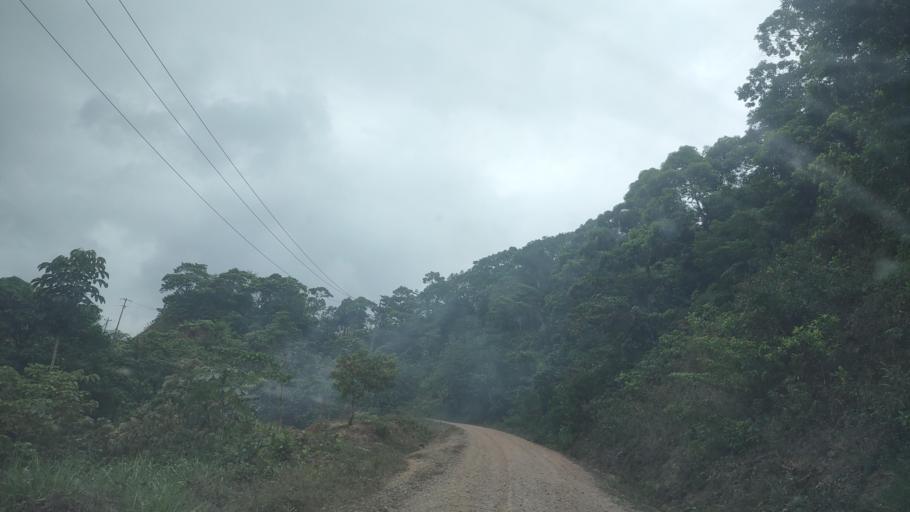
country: MX
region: Tabasco
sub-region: Huimanguillo
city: Francisco Rueda
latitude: 17.4393
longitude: -94.0245
